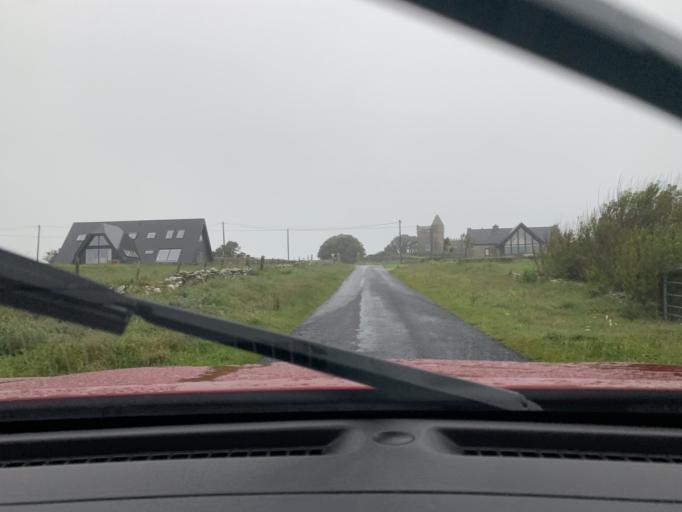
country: IE
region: Ulster
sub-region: County Donegal
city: Killybegs
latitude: 54.4688
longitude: -8.4544
